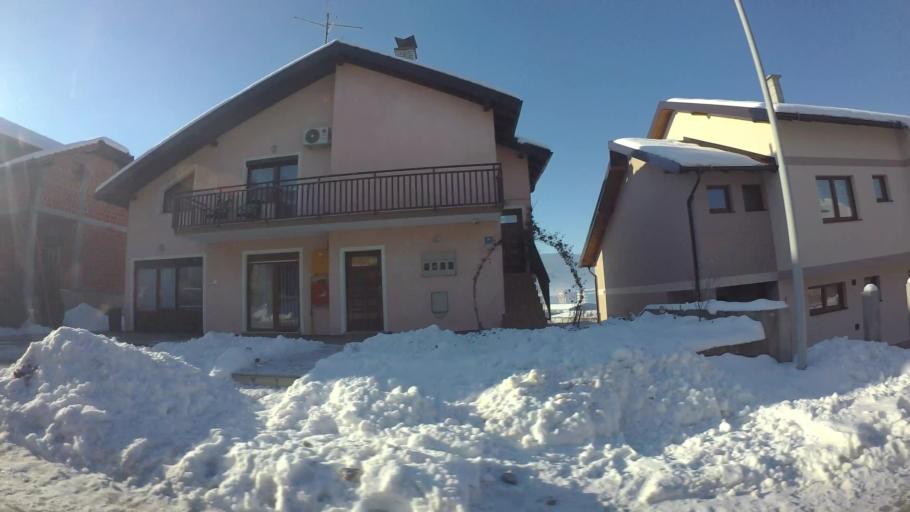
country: BA
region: Federation of Bosnia and Herzegovina
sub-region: Kanton Sarajevo
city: Sarajevo
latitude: 43.8201
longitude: 18.3689
